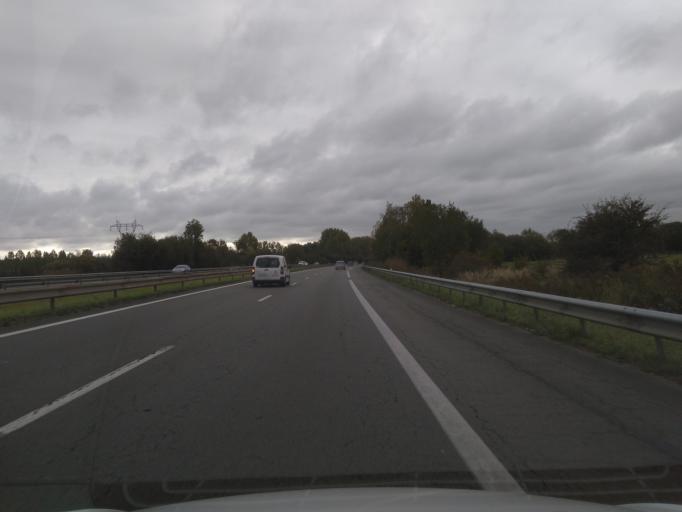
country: FR
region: Nord-Pas-de-Calais
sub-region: Departement du Nord
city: Genech
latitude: 50.5388
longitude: 3.1972
